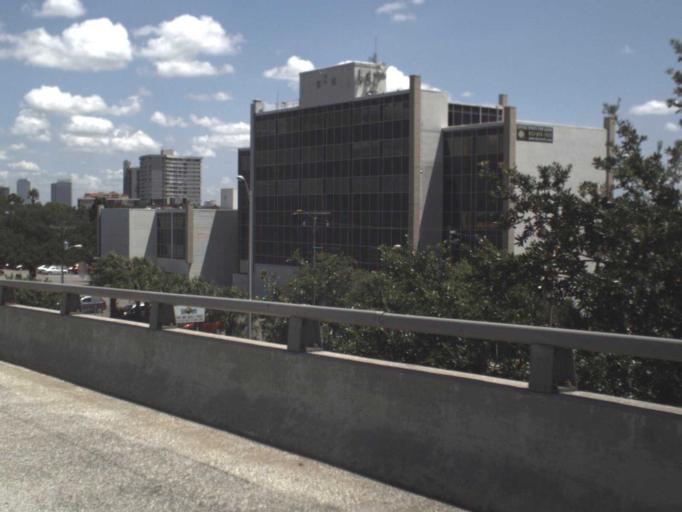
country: US
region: Florida
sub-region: Hillsborough County
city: Tampa
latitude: 27.9195
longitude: -82.4929
